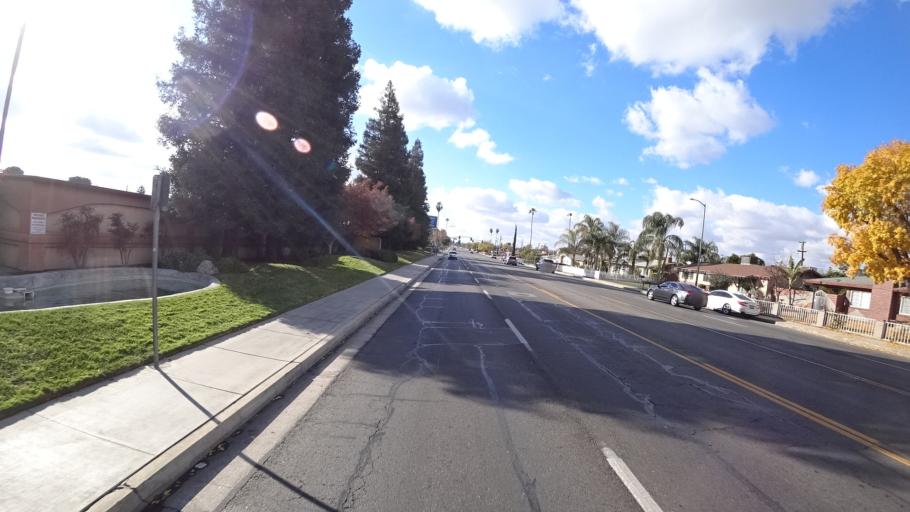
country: US
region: California
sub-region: Kern County
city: Bakersfield
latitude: 35.3322
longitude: -119.0462
